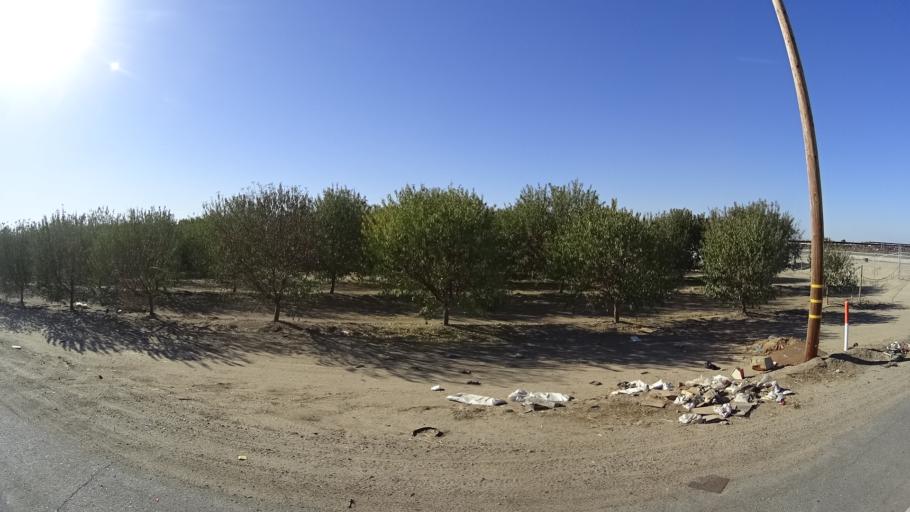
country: US
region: California
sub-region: Kern County
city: Greenfield
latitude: 35.2748
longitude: -118.9854
